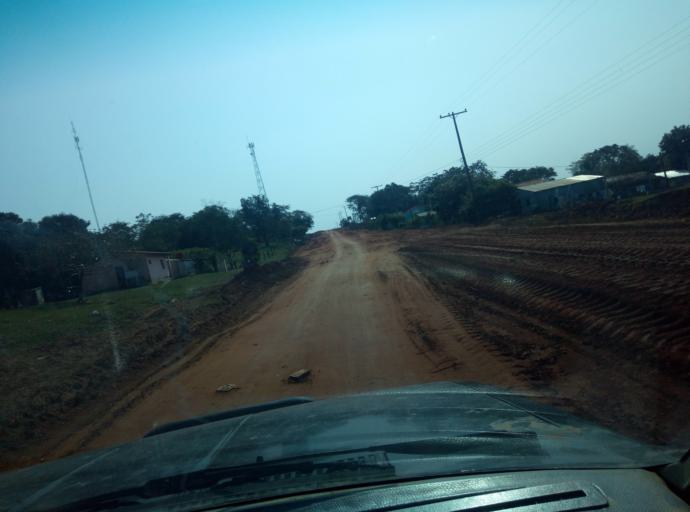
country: PY
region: Caaguazu
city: Carayao
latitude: -25.3174
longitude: -56.3280
